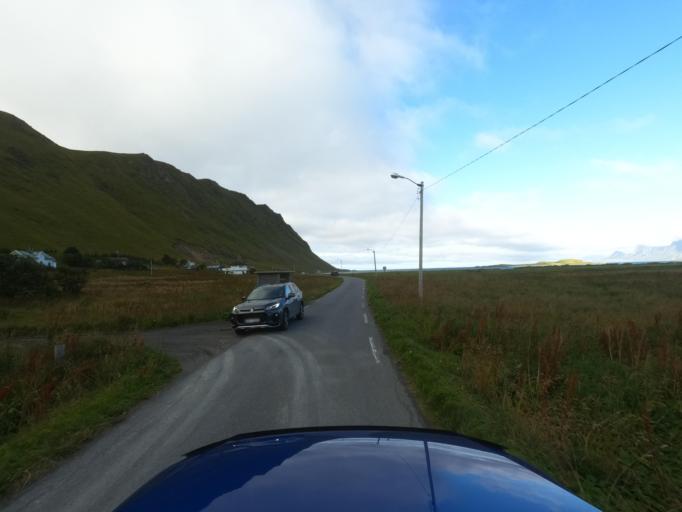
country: NO
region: Nordland
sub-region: Flakstad
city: Ramberg
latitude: 68.0958
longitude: 13.1372
